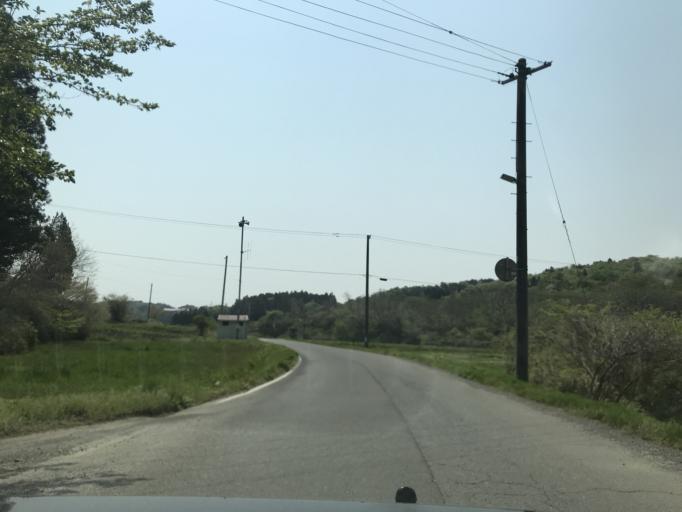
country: JP
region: Iwate
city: Ichinoseki
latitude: 38.8380
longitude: 141.0731
